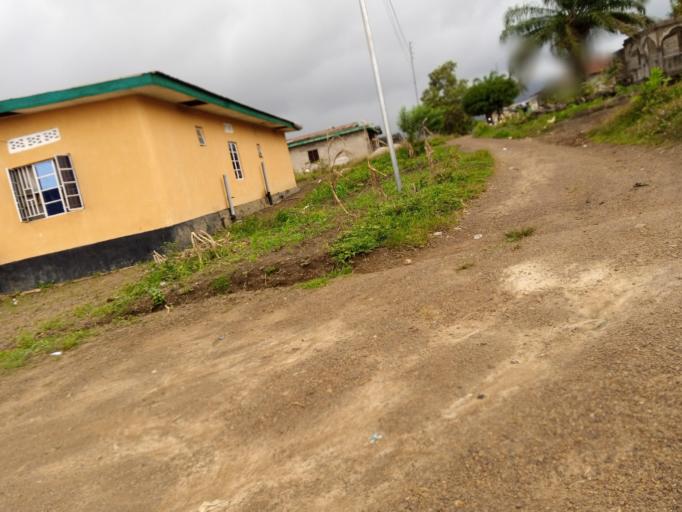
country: SL
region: Eastern Province
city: Kenema
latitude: 7.8794
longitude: -11.1743
